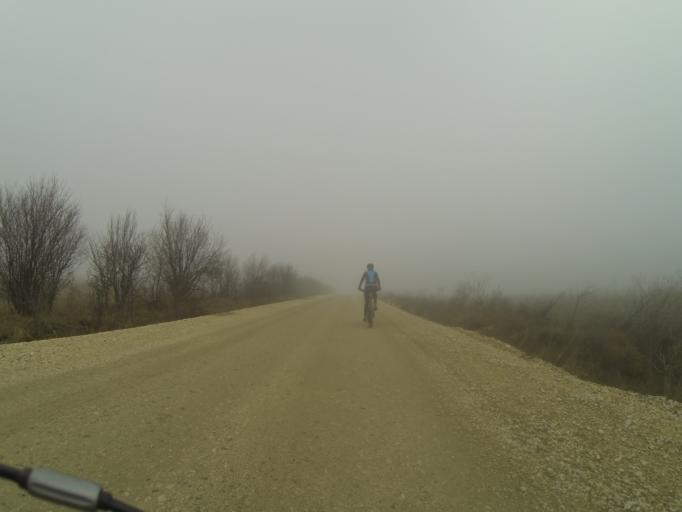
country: RO
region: Mehedinti
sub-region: Comuna Balacita
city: Gvardinita
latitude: 44.4353
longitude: 23.1345
